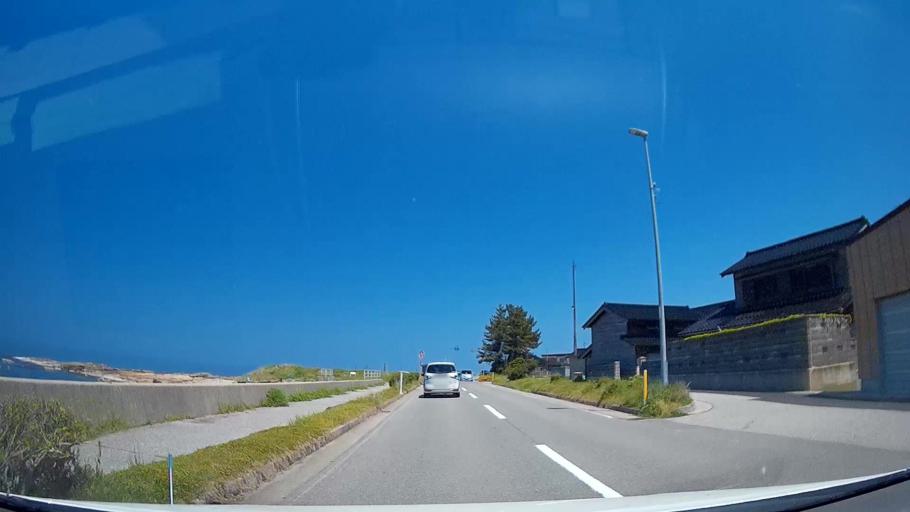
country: JP
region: Ishikawa
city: Nanao
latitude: 37.4827
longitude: 137.1077
